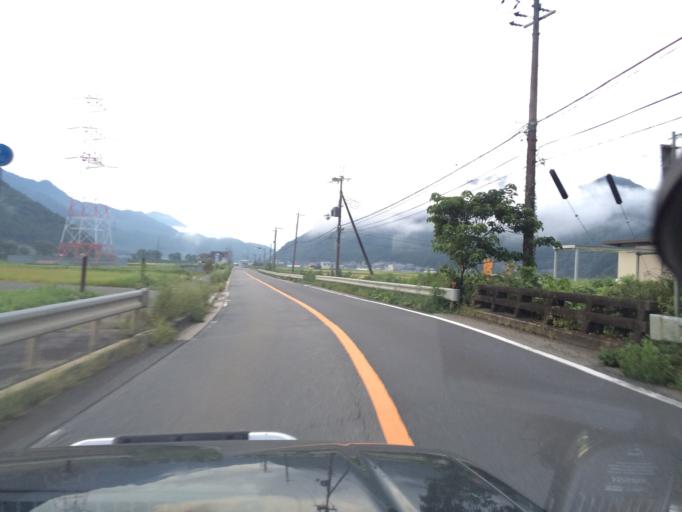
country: JP
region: Hyogo
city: Nishiwaki
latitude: 35.1137
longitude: 135.0010
